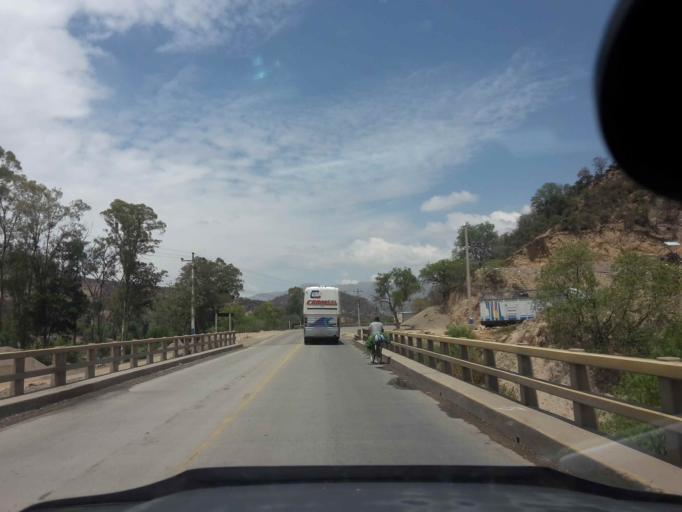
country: BO
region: Cochabamba
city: Sipe Sipe
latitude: -17.5417
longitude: -66.3364
